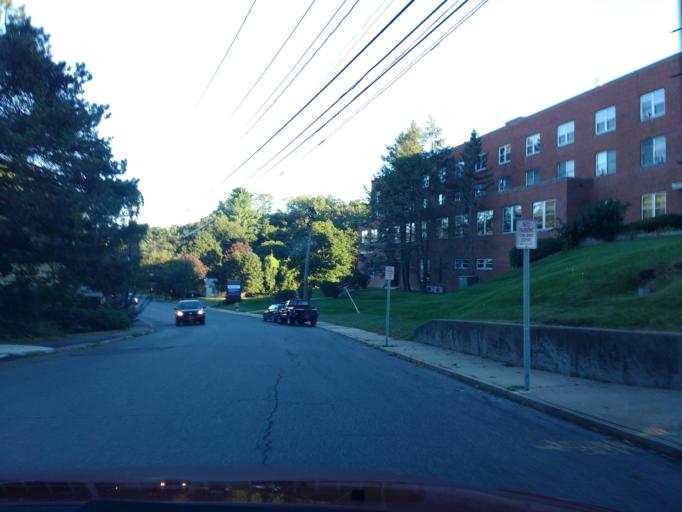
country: US
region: New York
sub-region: Ulster County
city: Kingston
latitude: 41.9221
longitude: -73.9990
